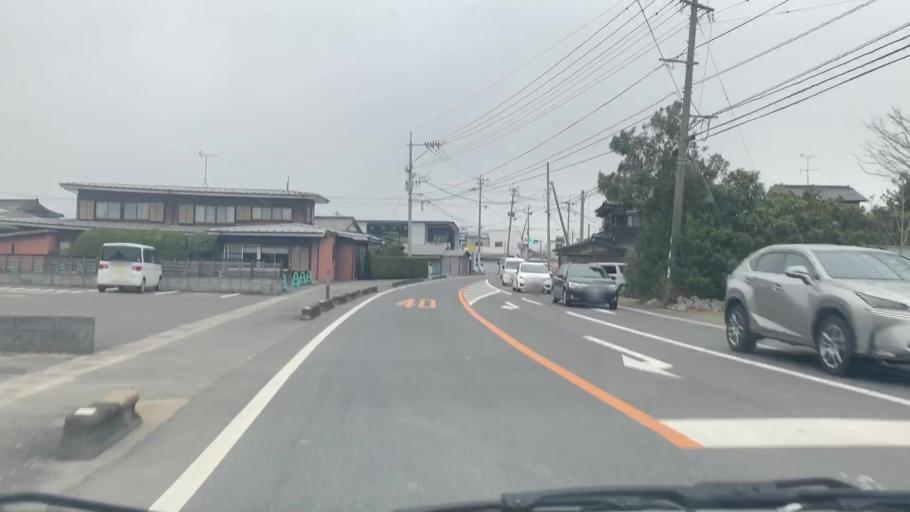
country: JP
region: Saga Prefecture
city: Saga-shi
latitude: 33.1956
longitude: 130.1929
